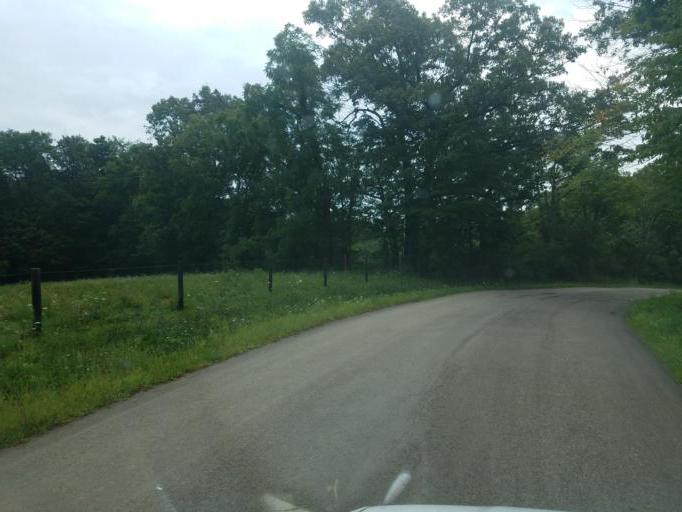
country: US
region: Ohio
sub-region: Knox County
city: Danville
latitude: 40.5526
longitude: -82.3597
